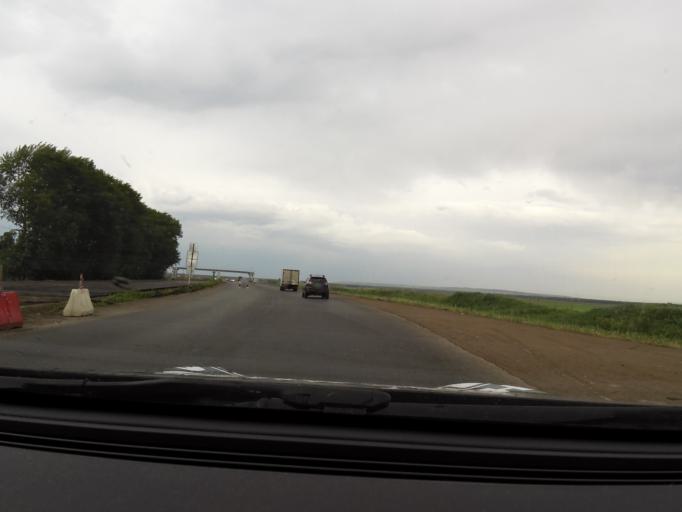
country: RU
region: Bashkortostan
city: Mikhaylovka
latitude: 54.8708
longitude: 55.7384
